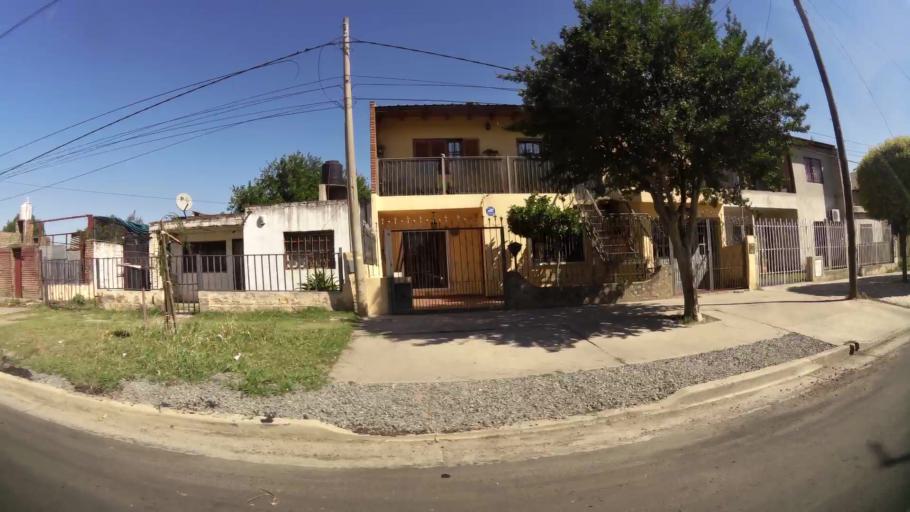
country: AR
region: Cordoba
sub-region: Departamento de Capital
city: Cordoba
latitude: -31.3686
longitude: -64.1602
